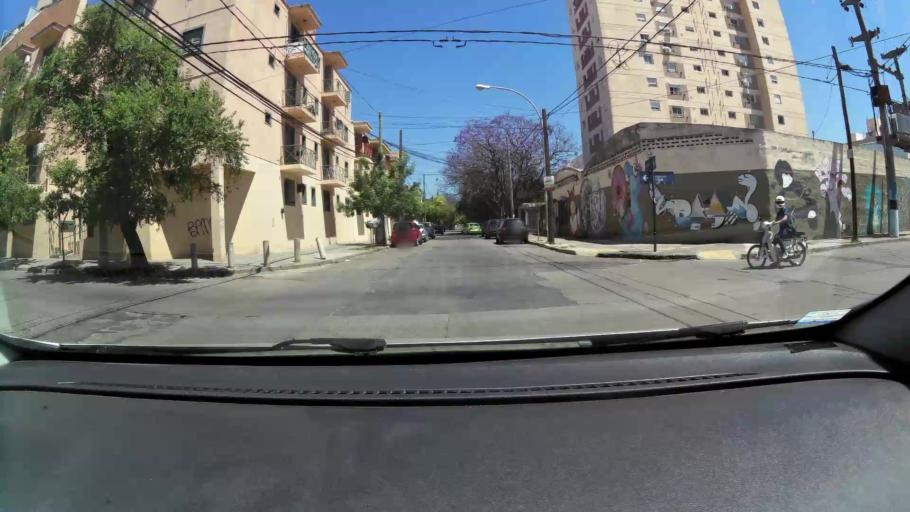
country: AR
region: Cordoba
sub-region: Departamento de Capital
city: Cordoba
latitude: -31.4093
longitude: -64.2095
